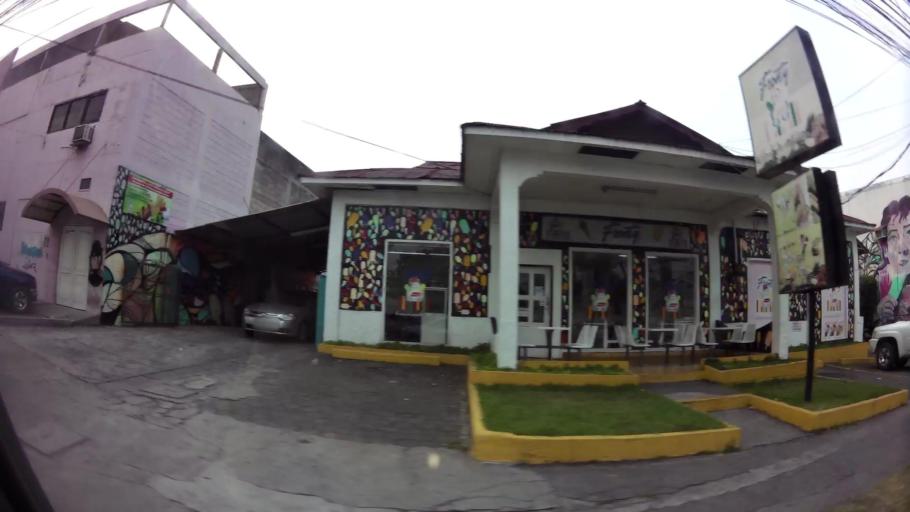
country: HN
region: Cortes
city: San Pedro Sula
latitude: 15.5065
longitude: -88.0317
